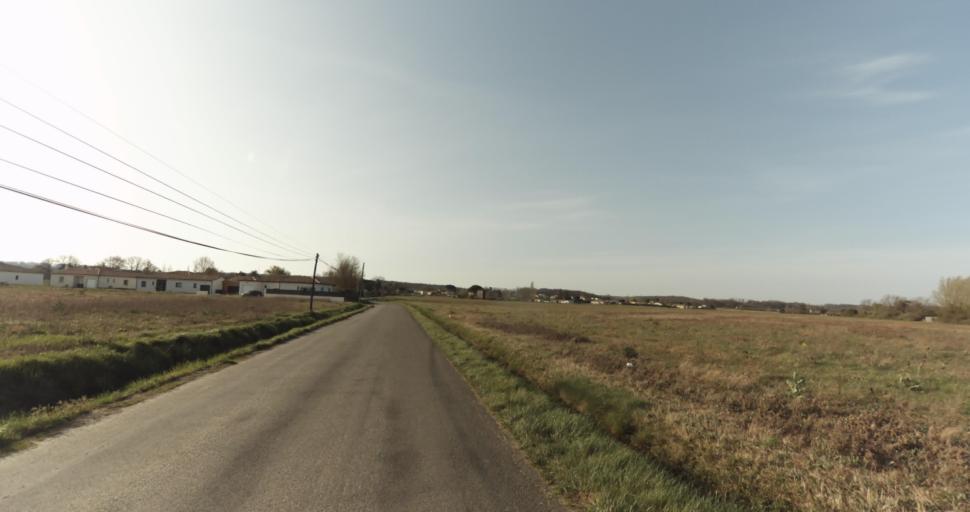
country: FR
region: Midi-Pyrenees
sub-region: Departement du Tarn
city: Saint-Sulpice-la-Pointe
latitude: 43.7637
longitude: 1.6773
